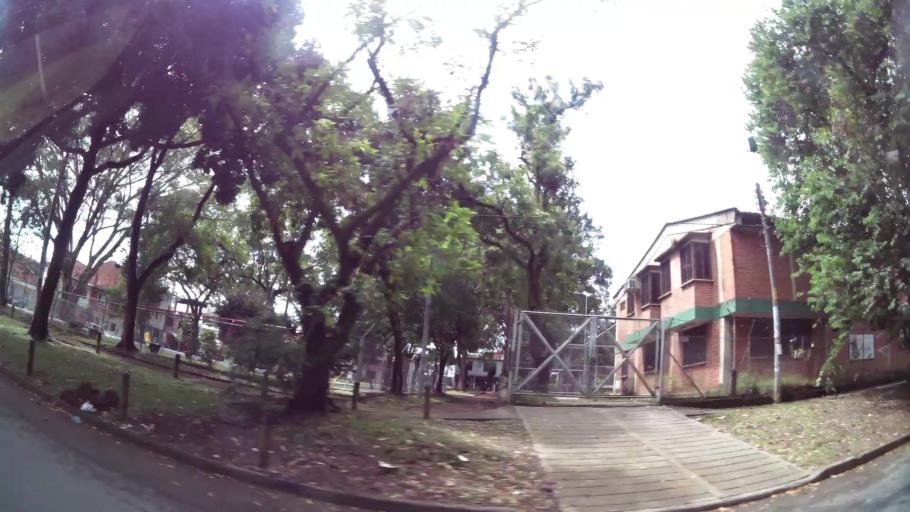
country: CO
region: Valle del Cauca
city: Cali
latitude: 3.3953
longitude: -76.5489
